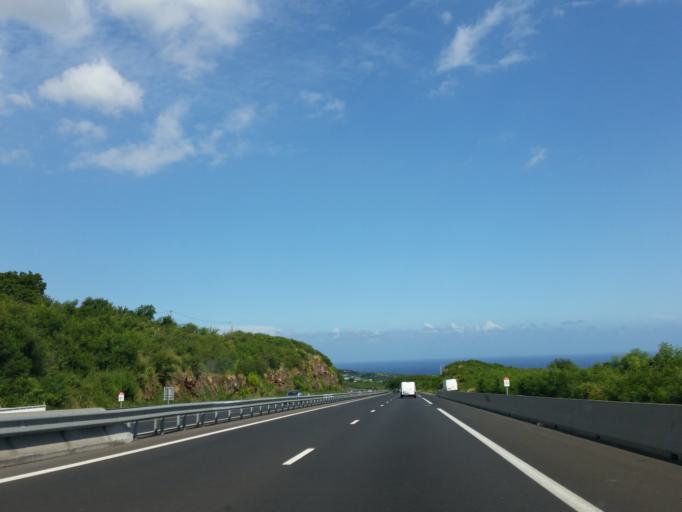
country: RE
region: Reunion
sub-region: Reunion
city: Saint-Leu
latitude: -21.1769
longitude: 55.2970
